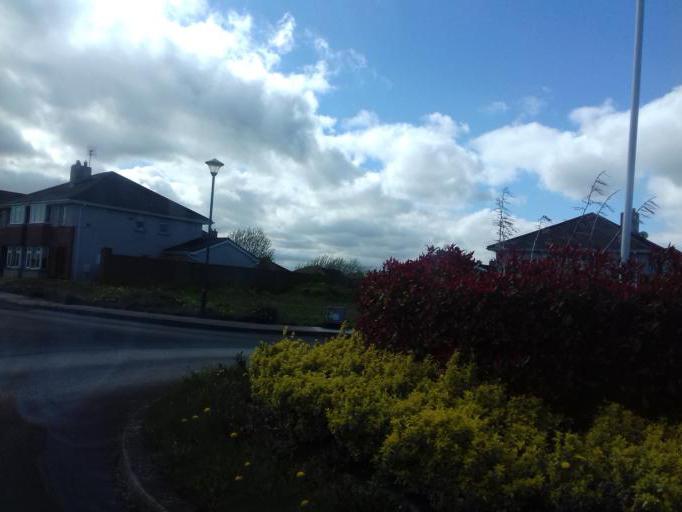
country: IE
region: Leinster
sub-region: Laois
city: Portlaoise
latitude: 53.0480
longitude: -7.2633
